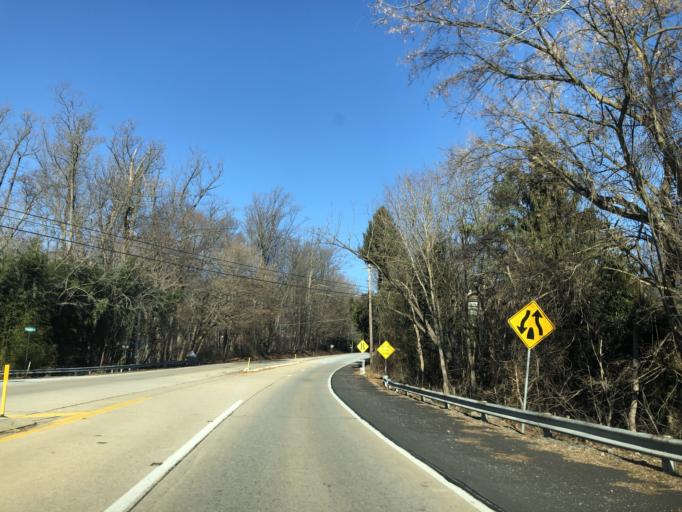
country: US
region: Pennsylvania
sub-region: Chester County
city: Kennett Square
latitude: 39.8576
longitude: -75.7156
